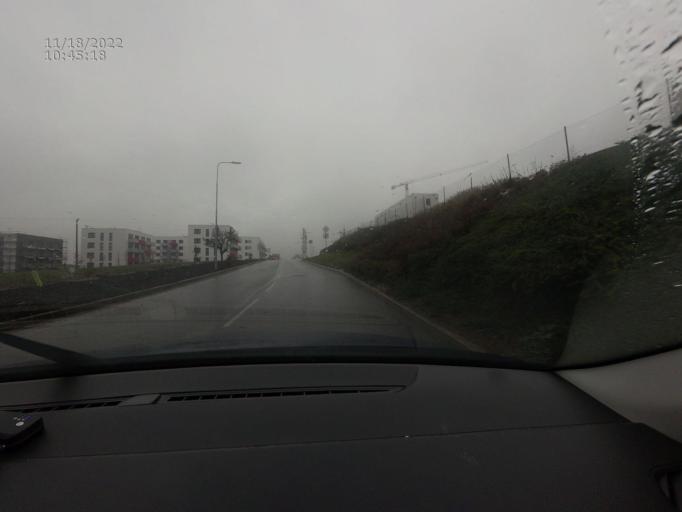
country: CZ
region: Central Bohemia
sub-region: Okres Beroun
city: Horovice
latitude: 49.8425
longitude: 13.9156
